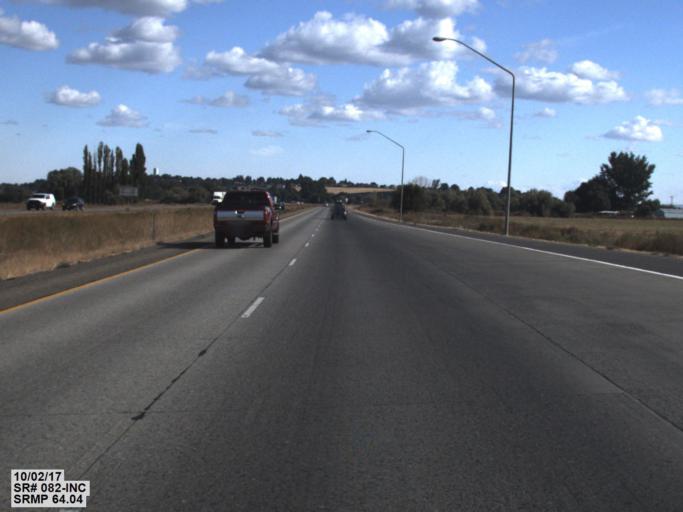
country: US
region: Washington
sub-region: Yakima County
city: Sunnyside
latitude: 46.3233
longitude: -120.0713
